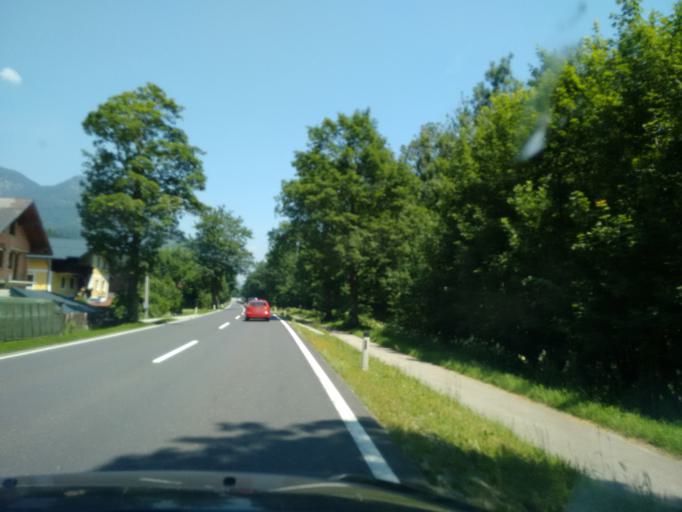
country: AT
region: Upper Austria
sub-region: Politischer Bezirk Gmunden
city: Ebensee
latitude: 47.7697
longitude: 13.7220
